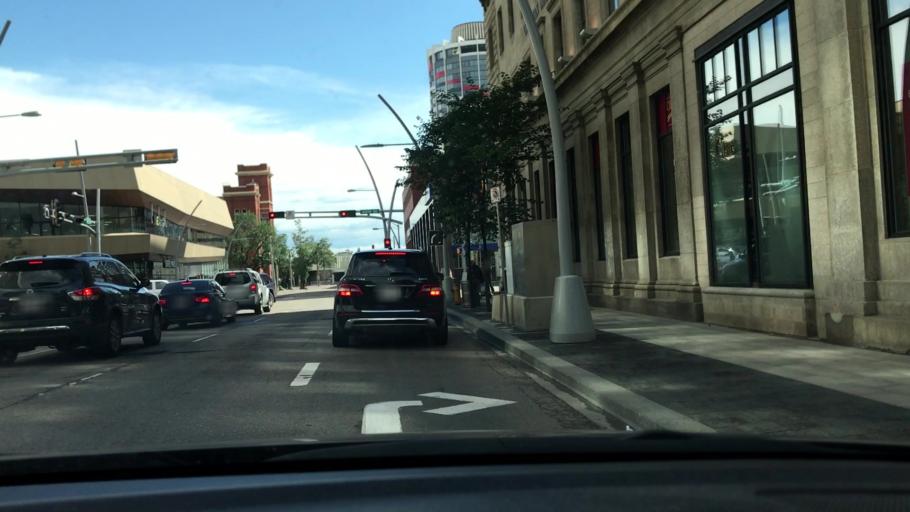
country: CA
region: Alberta
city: Edmonton
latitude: 53.5414
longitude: -113.4938
